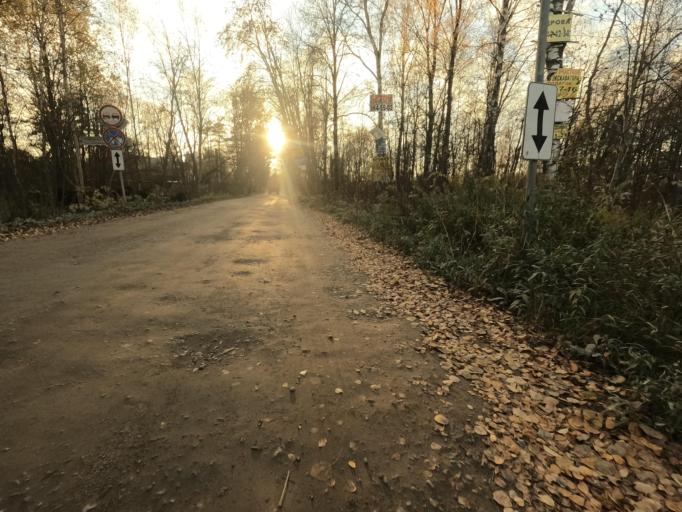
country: RU
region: St.-Petersburg
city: Beloostrov
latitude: 60.1810
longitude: 30.0439
